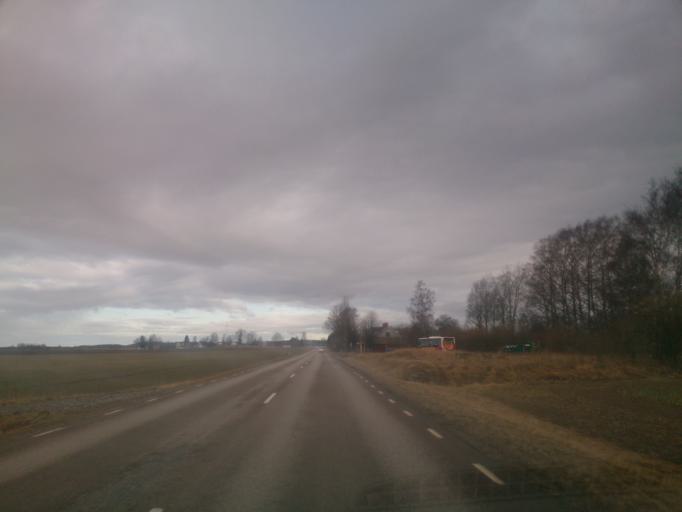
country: SE
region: OEstergoetland
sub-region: Motala Kommun
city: Borensberg
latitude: 58.5167
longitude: 15.1787
